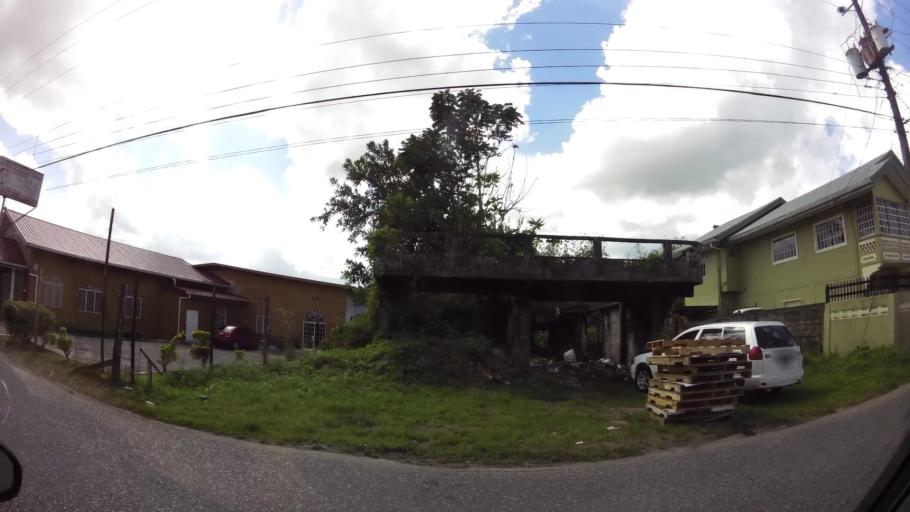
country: TT
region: Penal/Debe
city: Debe
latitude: 10.2368
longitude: -61.4401
